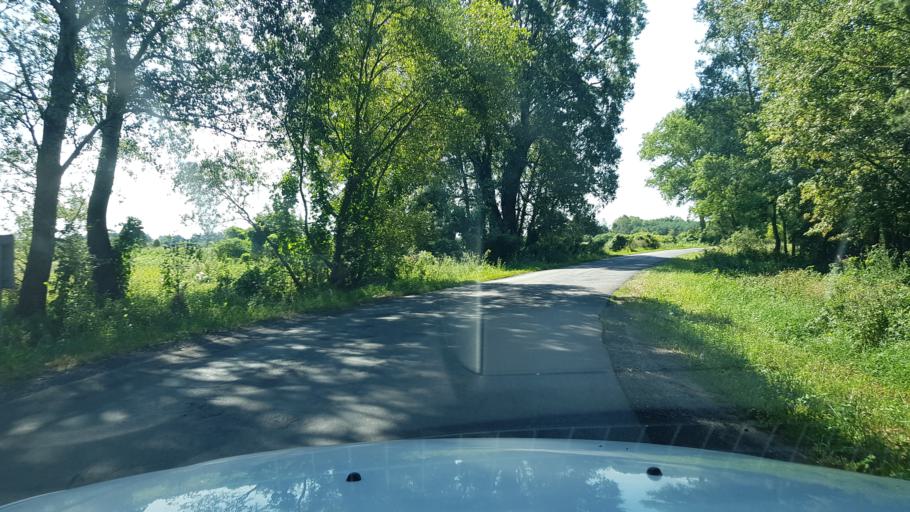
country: PL
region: West Pomeranian Voivodeship
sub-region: Powiat goleniowski
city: Goleniow
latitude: 53.4730
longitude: 14.7165
